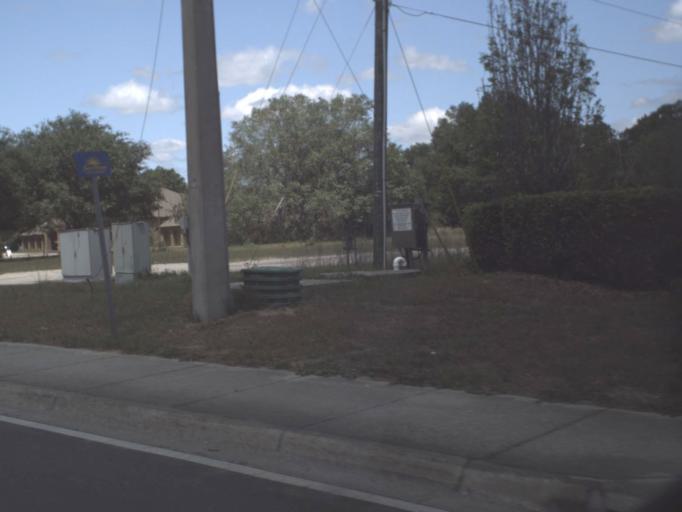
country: US
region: Florida
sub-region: Marion County
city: Ocala
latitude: 29.2085
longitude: -82.0700
